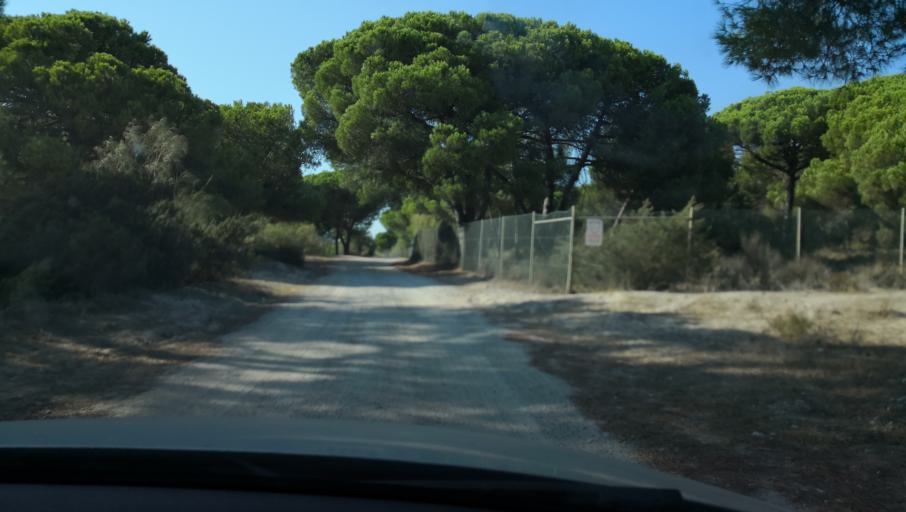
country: PT
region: Setubal
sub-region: Setubal
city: Setubal
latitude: 38.4846
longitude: -8.8825
